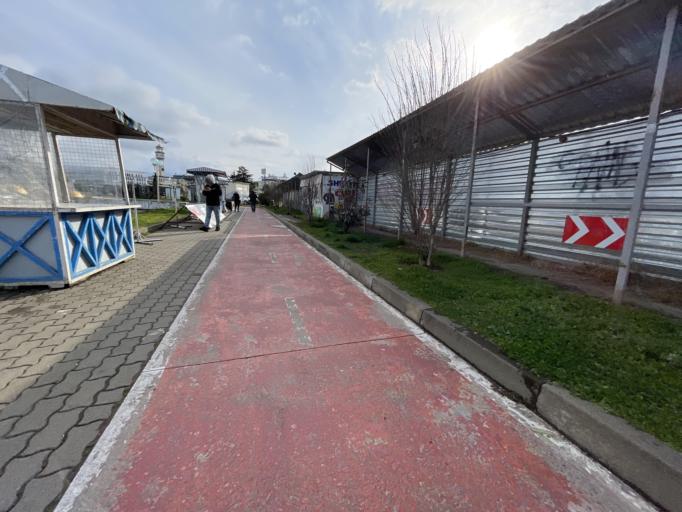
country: GE
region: Ajaria
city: Batumi
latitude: 41.6545
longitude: 41.6428
